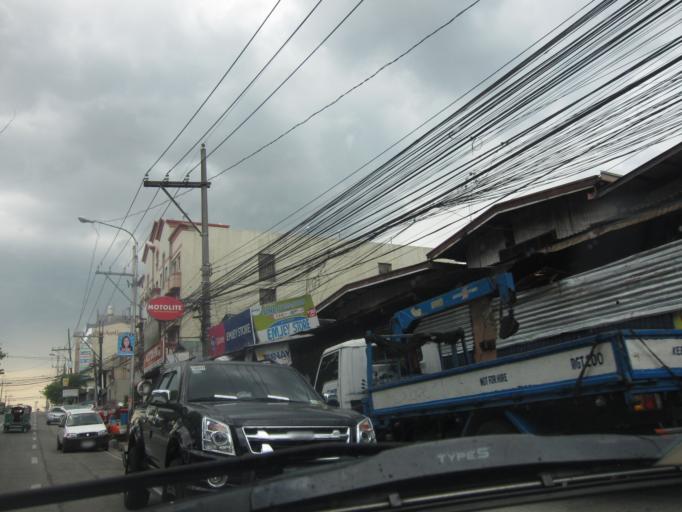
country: PH
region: Metro Manila
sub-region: Quezon City
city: Quezon City
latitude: 14.6369
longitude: 121.0514
